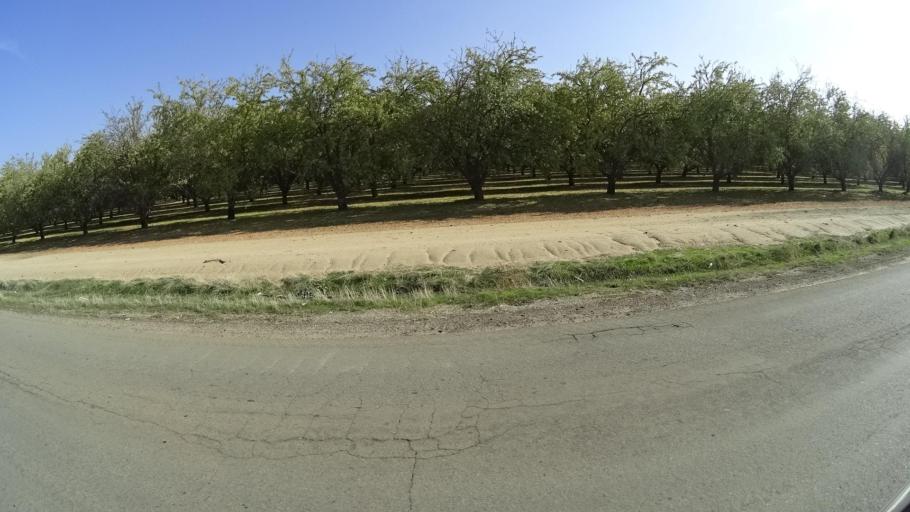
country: US
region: California
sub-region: Kern County
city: McFarland
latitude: 35.6443
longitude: -119.1691
